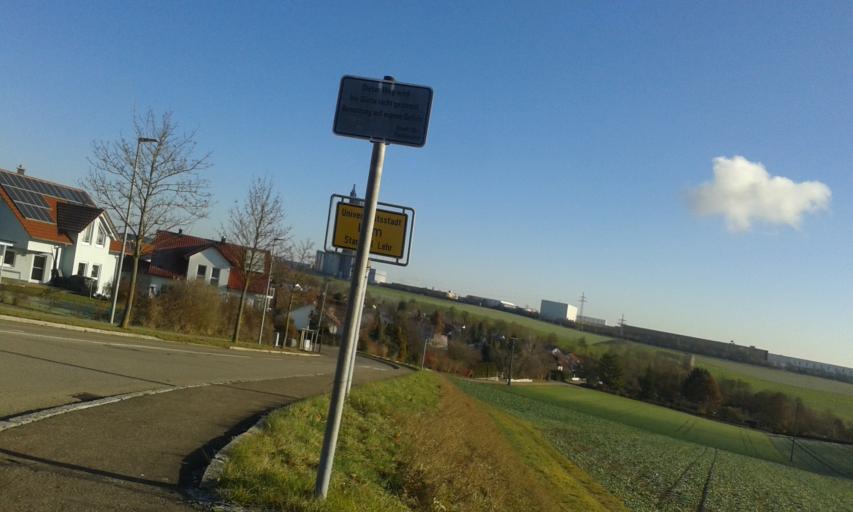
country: DE
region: Baden-Wuerttemberg
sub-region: Tuebingen Region
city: Ulm
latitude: 48.4290
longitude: 9.9695
